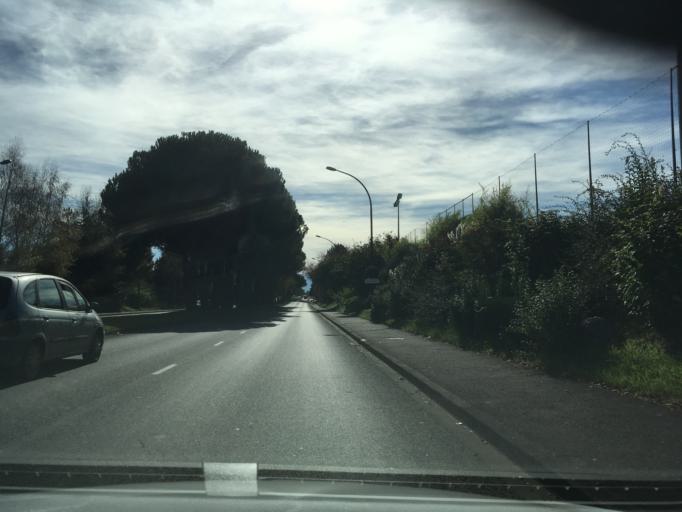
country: FR
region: Aquitaine
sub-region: Departement des Pyrenees-Atlantiques
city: Pau
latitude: 43.3244
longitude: -0.3577
